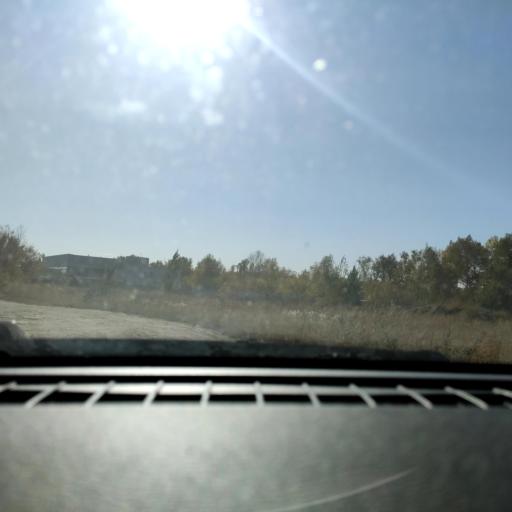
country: RU
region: Voronezj
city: Somovo
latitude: 51.6679
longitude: 39.2996
